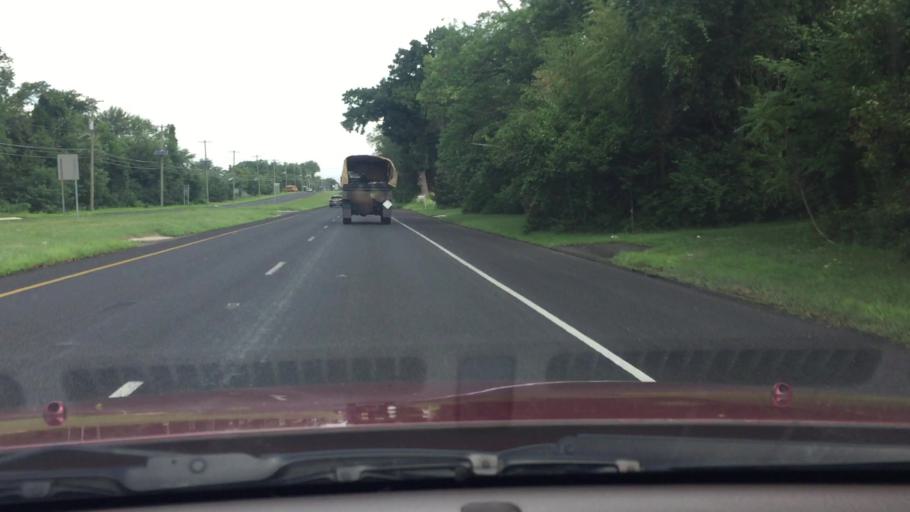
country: US
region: New Jersey
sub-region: Burlington County
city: Bordentown
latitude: 40.0906
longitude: -74.6780
